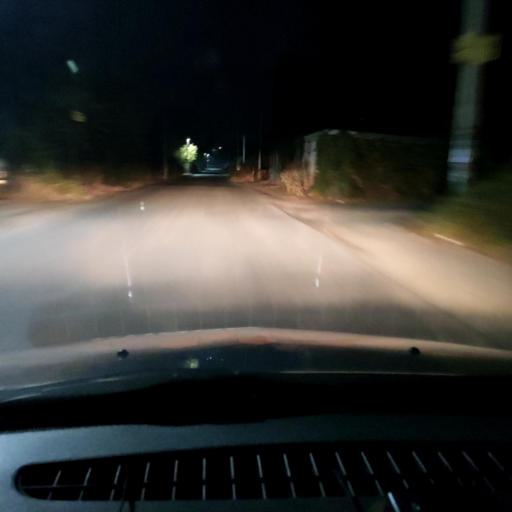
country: RU
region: Voronezj
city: Shilovo
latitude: 51.5940
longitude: 39.1546
